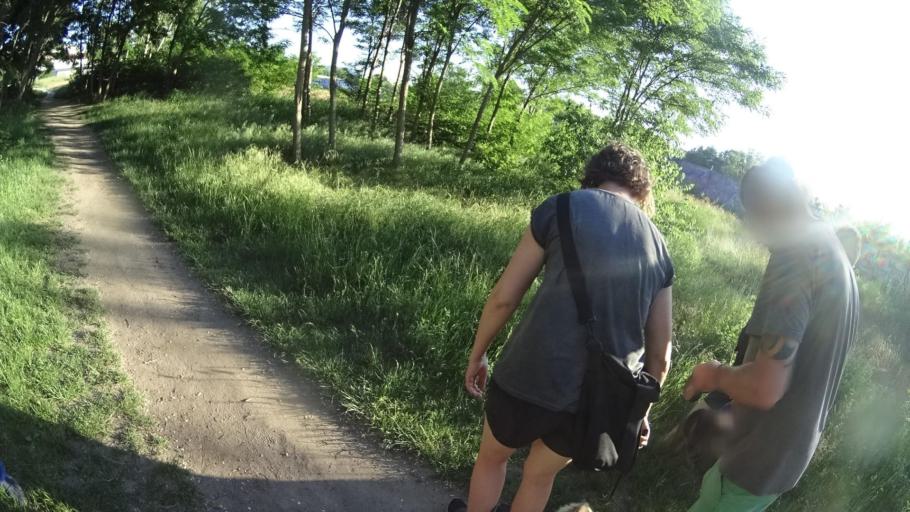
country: PL
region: Masovian Voivodeship
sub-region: Warszawa
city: Bemowo
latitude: 52.2602
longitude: 20.9142
